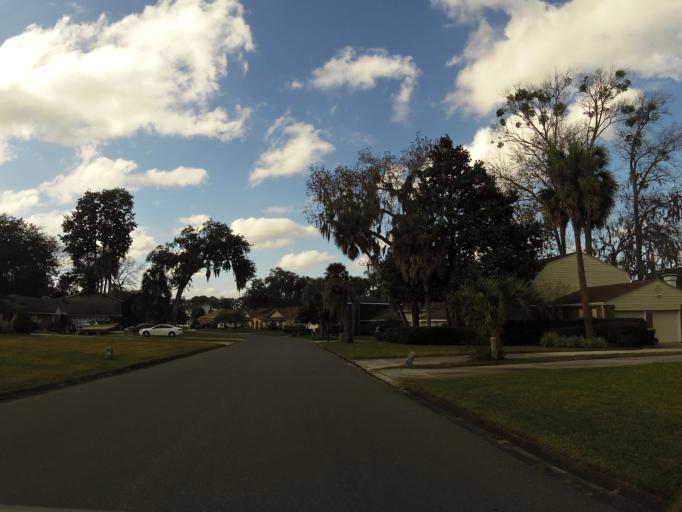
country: US
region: Florida
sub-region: Duval County
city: Atlantic Beach
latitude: 30.3773
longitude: -81.5145
